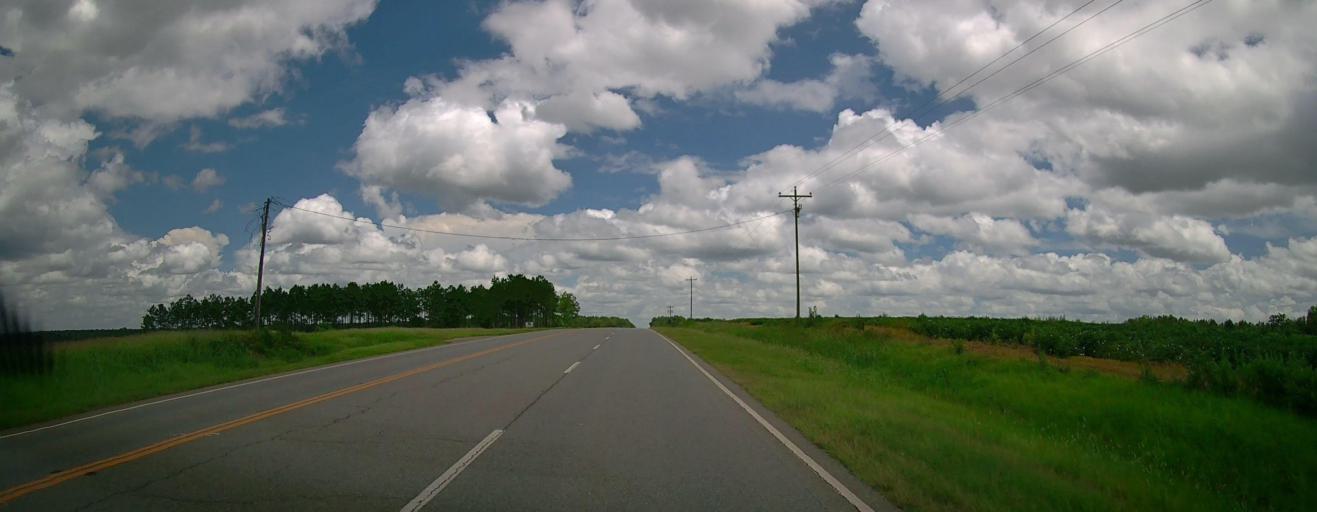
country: US
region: Georgia
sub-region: Turner County
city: Ashburn
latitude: 31.7220
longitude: -83.5379
